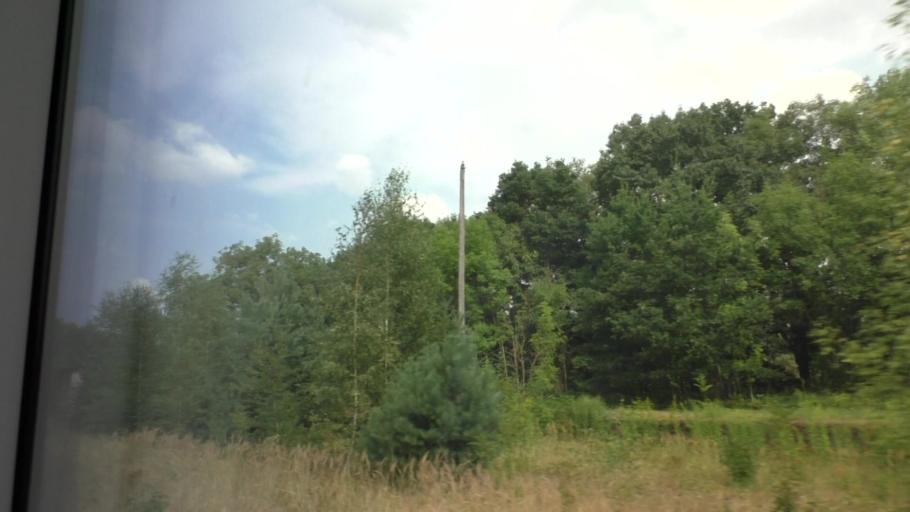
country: DE
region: Brandenburg
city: Mixdorf
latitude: 52.1682
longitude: 14.3796
